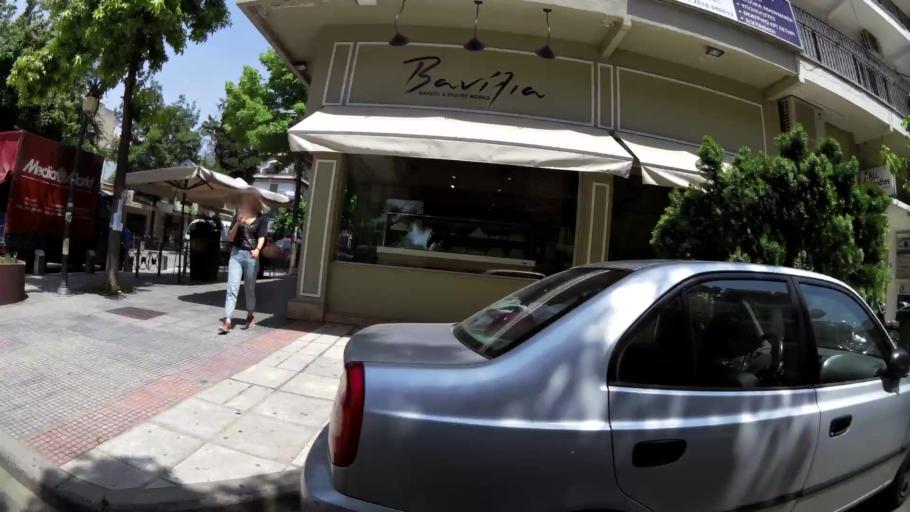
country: GR
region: Central Macedonia
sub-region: Nomos Thessalonikis
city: Menemeni
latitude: 40.6717
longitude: 22.8942
